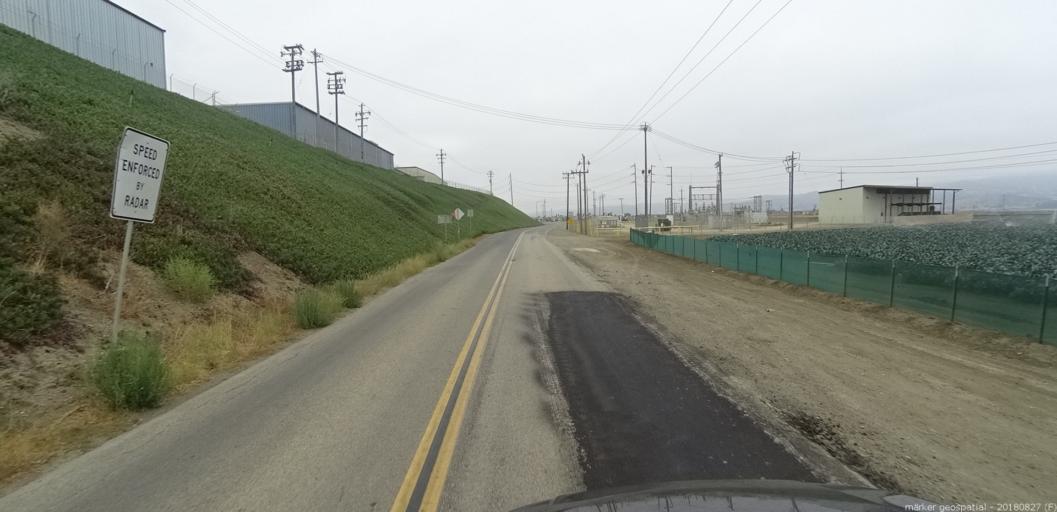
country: US
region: California
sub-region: Monterey County
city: King City
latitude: 36.2294
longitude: -121.1291
